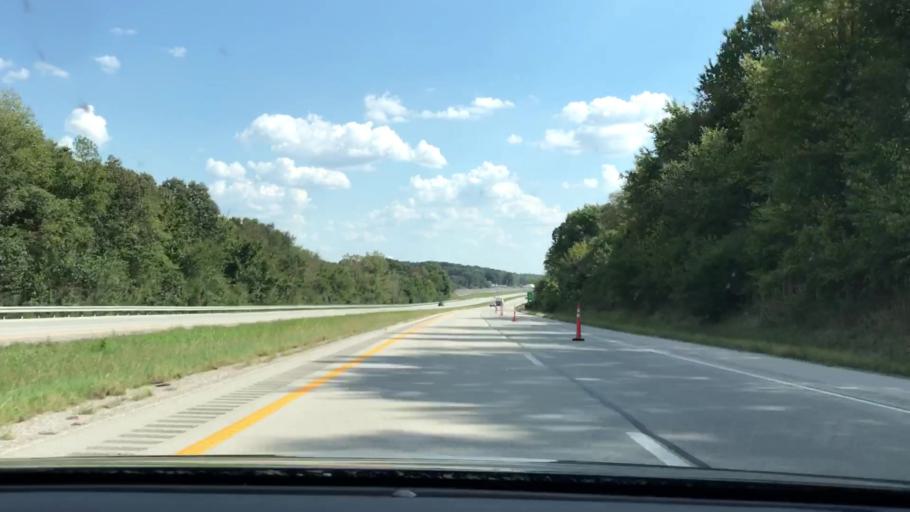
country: US
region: Kentucky
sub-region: Butler County
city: Morgantown
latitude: 37.2217
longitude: -86.7165
